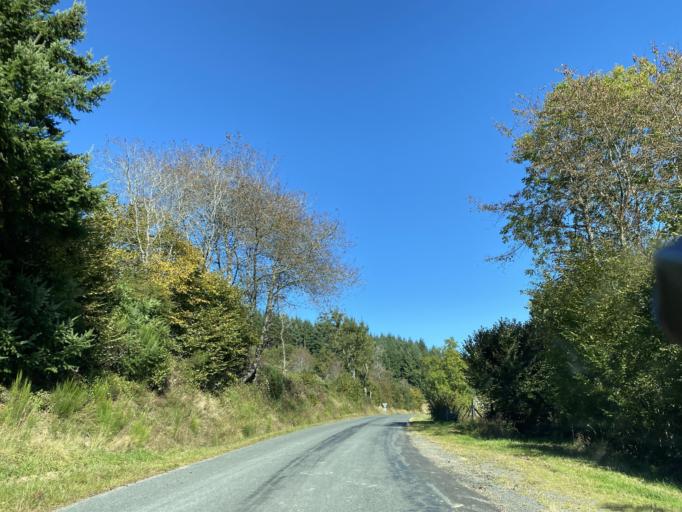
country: FR
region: Rhone-Alpes
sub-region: Departement de la Loire
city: Saint-Just-en-Chevalet
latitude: 45.9536
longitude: 3.8788
